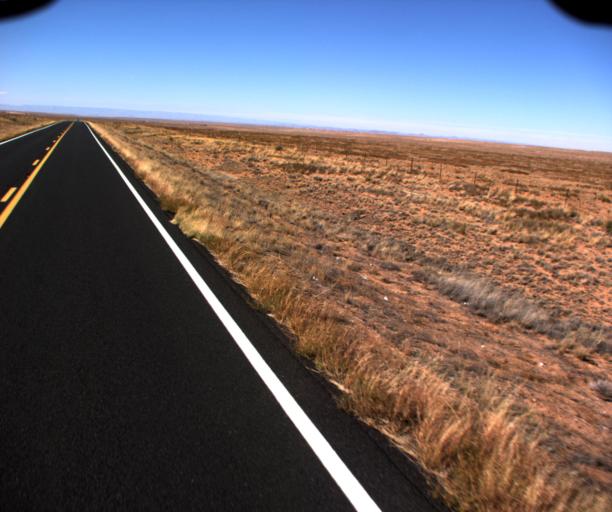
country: US
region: Arizona
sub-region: Coconino County
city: Tuba City
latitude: 36.0112
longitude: -111.0718
